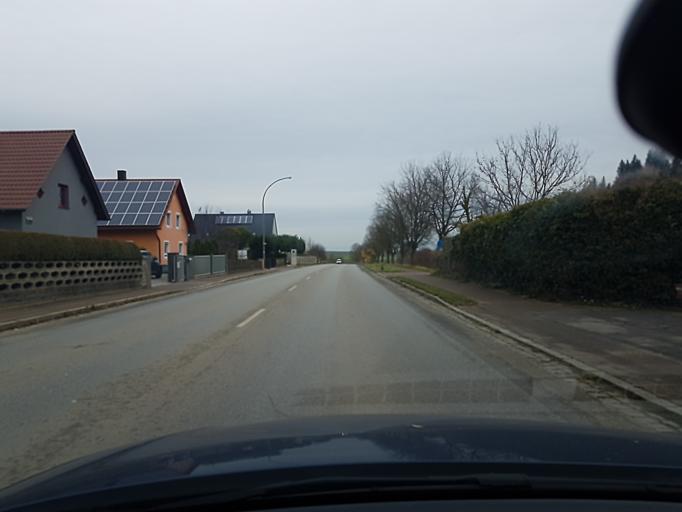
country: DE
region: Bavaria
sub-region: Upper Palatinate
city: Hagelstadt
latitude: 48.9000
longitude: 12.2129
